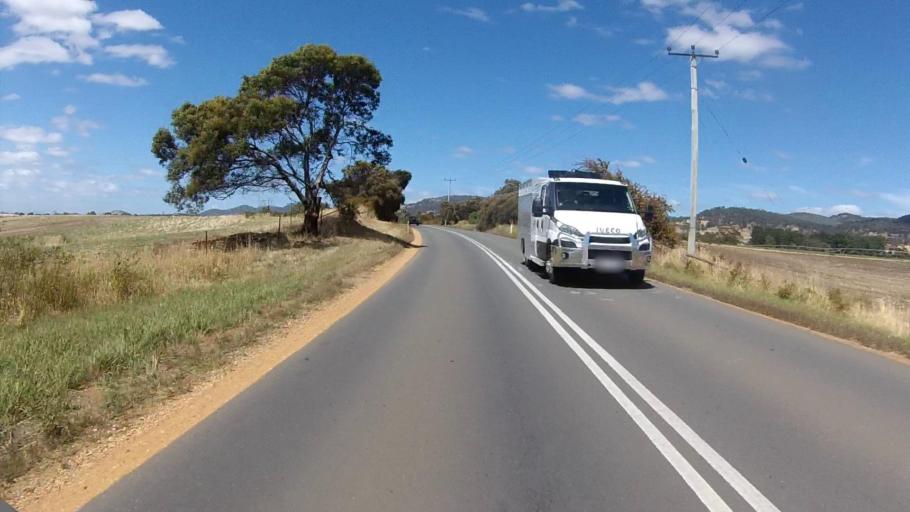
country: AU
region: Tasmania
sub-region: Clarence
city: Cambridge
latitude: -42.7628
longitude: 147.4149
